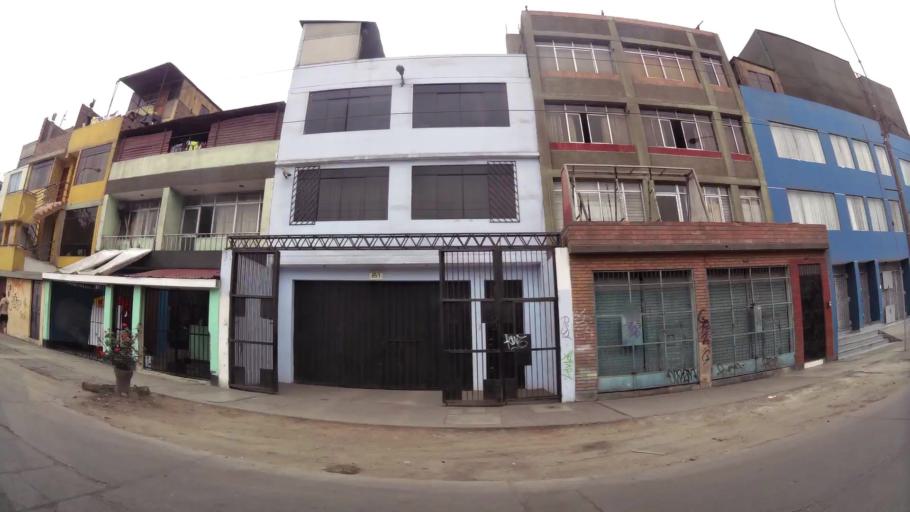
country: PE
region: Lima
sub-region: Lima
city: San Luis
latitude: -12.0745
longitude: -77.0013
